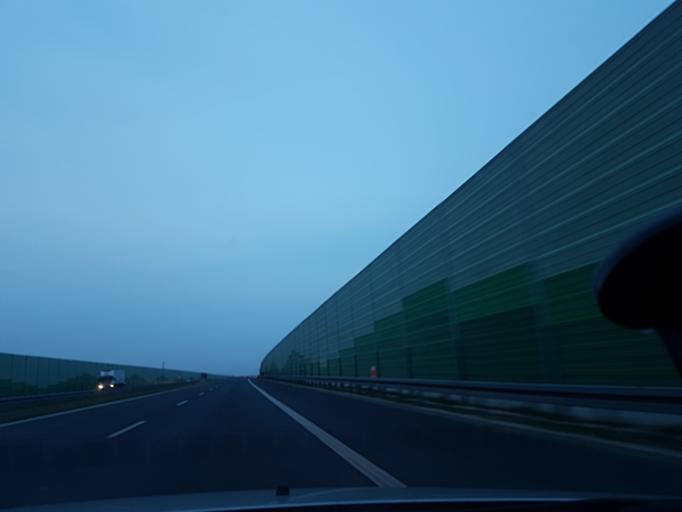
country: PL
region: Lodz Voivodeship
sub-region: Powiat leczycki
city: Piatek
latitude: 52.1131
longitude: 19.5060
